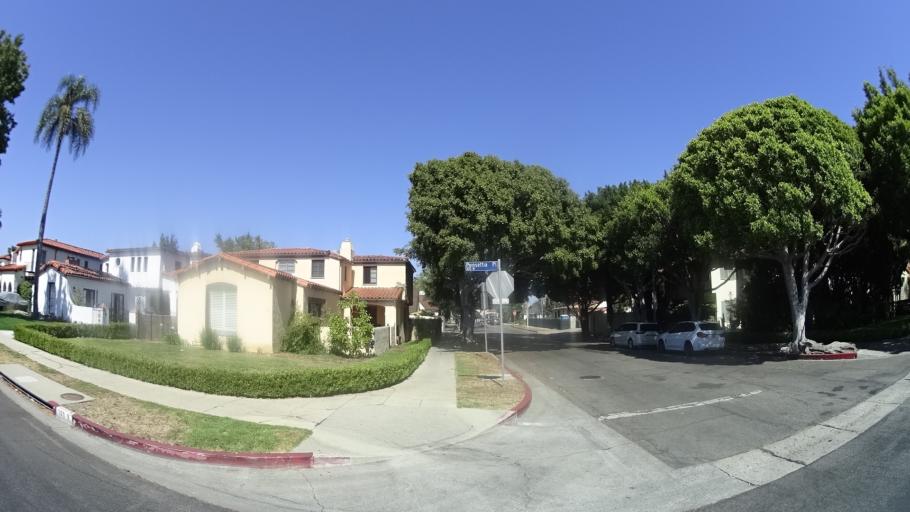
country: US
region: California
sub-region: Los Angeles County
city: West Hollywood
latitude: 34.0736
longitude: -118.3486
